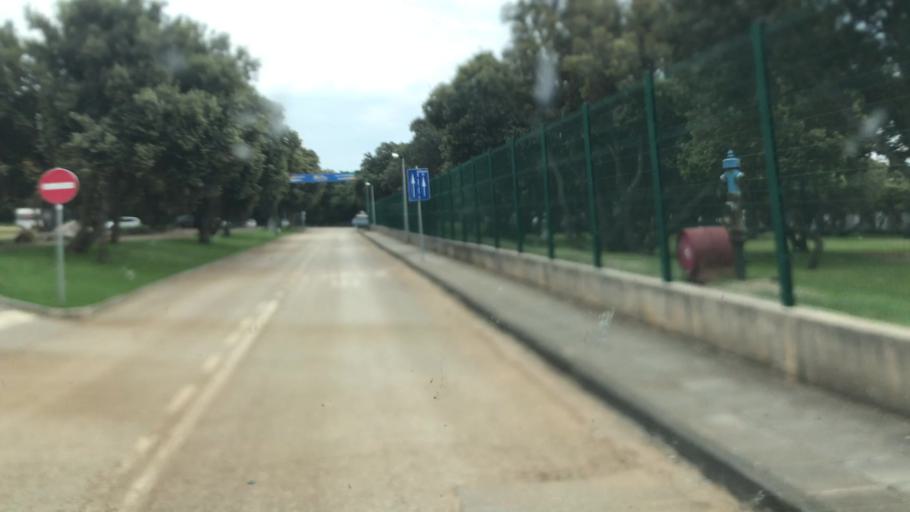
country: HR
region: Licko-Senjska
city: Novalja
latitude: 44.5400
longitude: 14.8856
